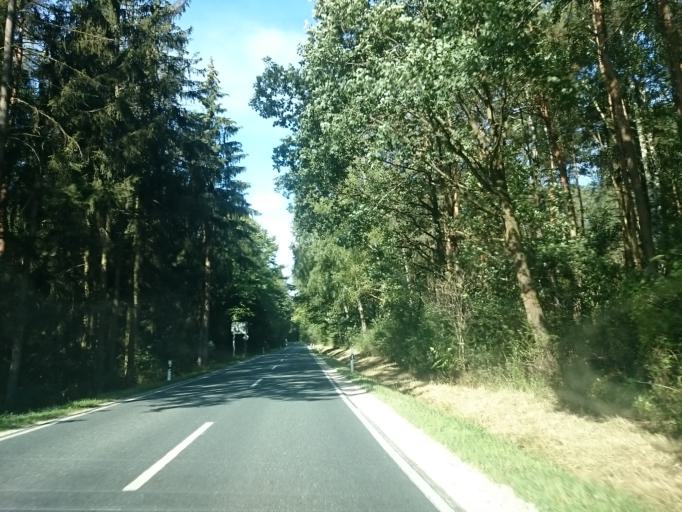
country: DE
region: Bavaria
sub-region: Regierungsbezirk Mittelfranken
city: Rottenbach
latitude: 49.1317
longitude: 11.0740
